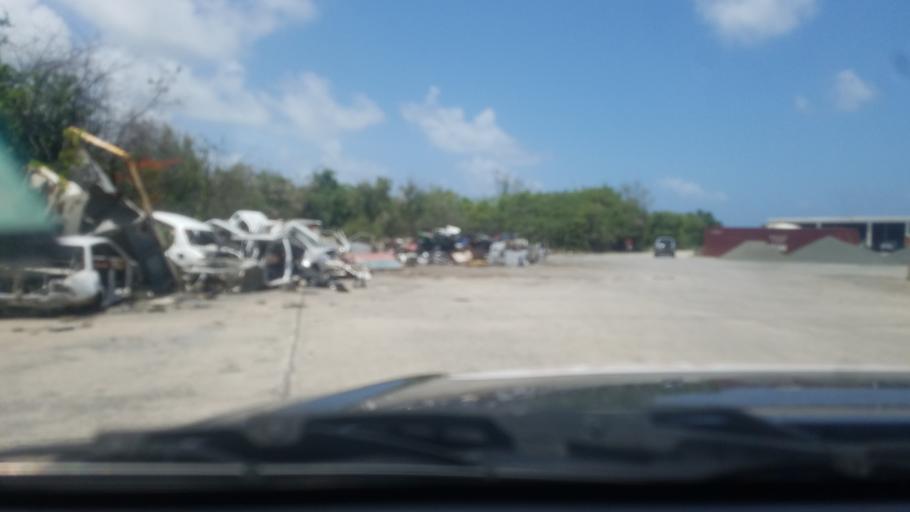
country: LC
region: Vieux-Fort
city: Vieux Fort
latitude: 13.7458
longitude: -60.9462
